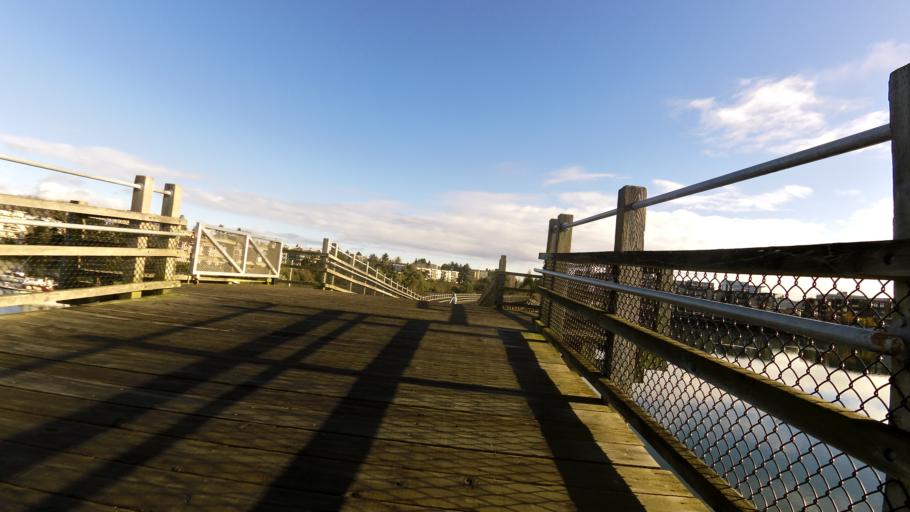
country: CA
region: British Columbia
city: Victoria
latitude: 48.4389
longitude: -123.3827
